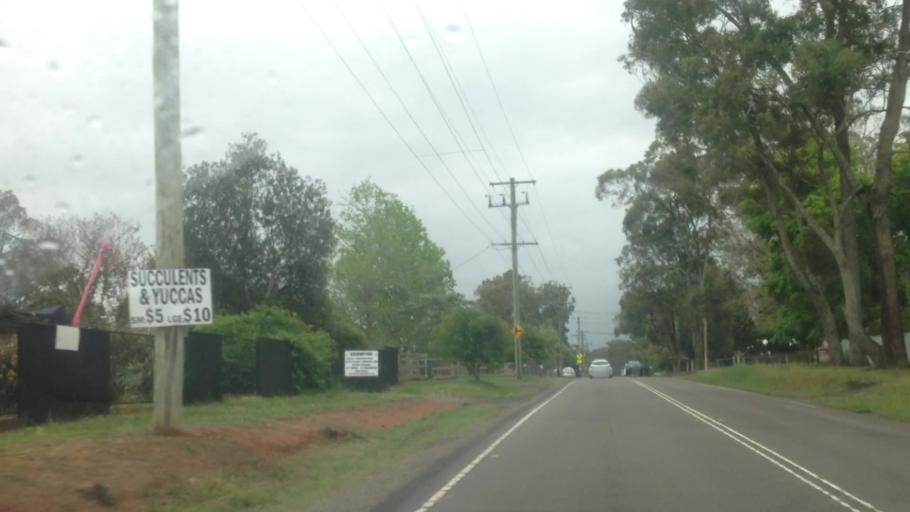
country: AU
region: New South Wales
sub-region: Lake Macquarie Shire
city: Dora Creek
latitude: -33.0988
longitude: 151.4734
